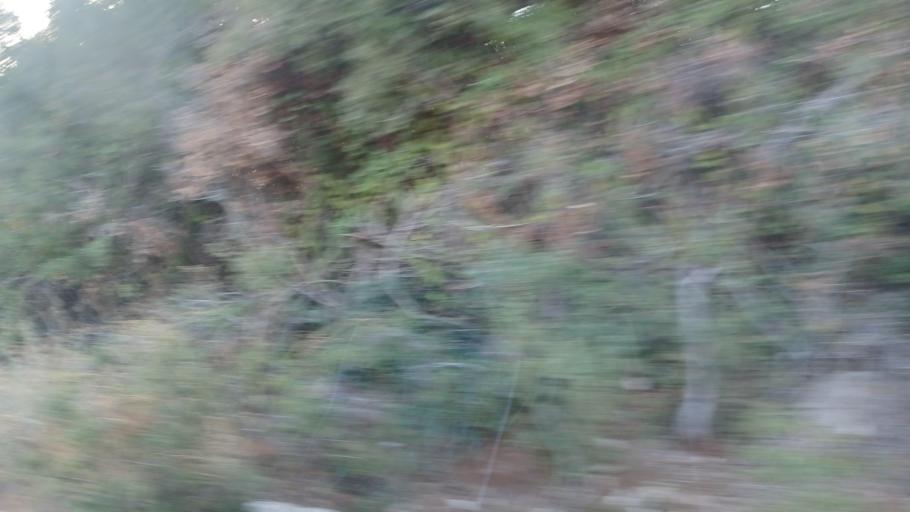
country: CY
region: Pafos
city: Polis
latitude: 34.9757
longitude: 32.4280
